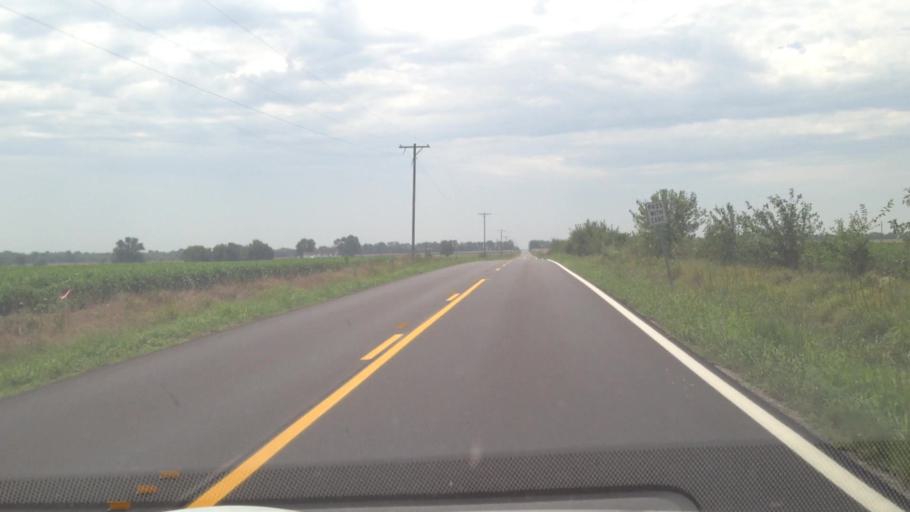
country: US
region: Kansas
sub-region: Crawford County
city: Girard
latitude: 37.6487
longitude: -94.9698
